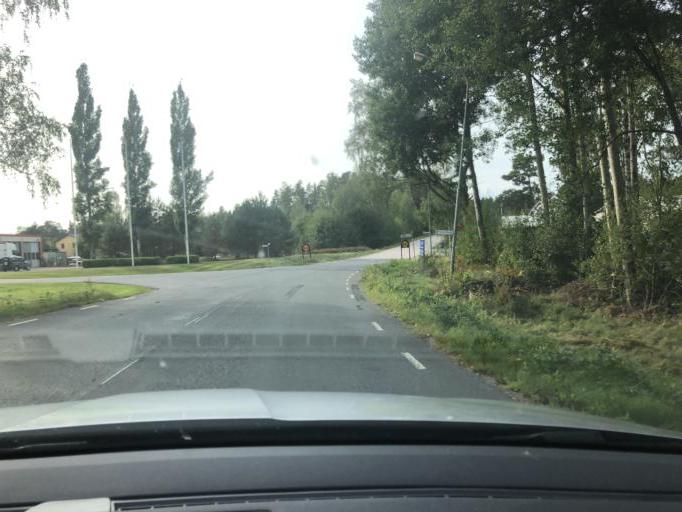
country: SE
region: Joenkoeping
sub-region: Vetlanda Kommun
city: Ekenassjon
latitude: 57.5218
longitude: 14.9116
